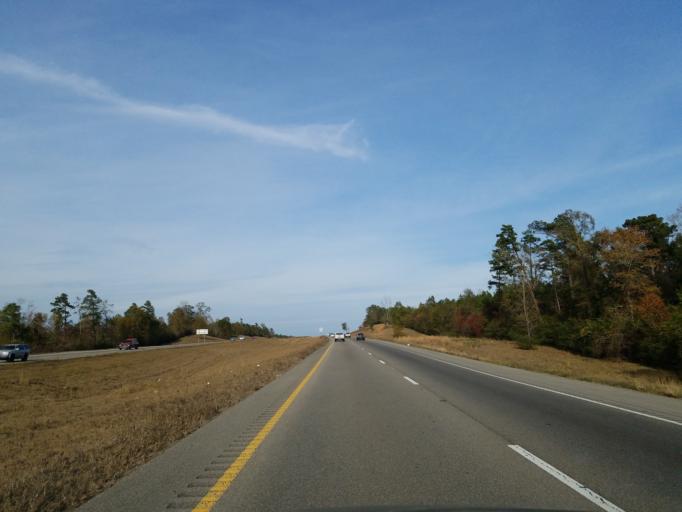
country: US
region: Mississippi
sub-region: Jones County
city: Ellisville
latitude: 31.5279
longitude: -89.2805
